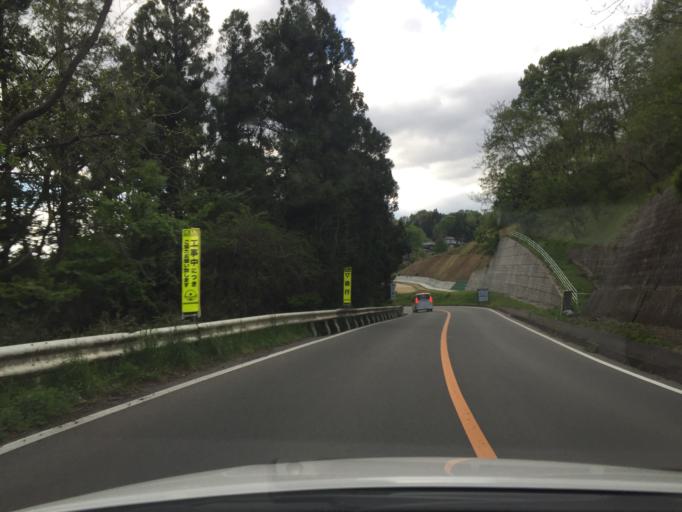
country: JP
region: Fukushima
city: Fukushima-shi
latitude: 37.6615
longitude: 140.5078
